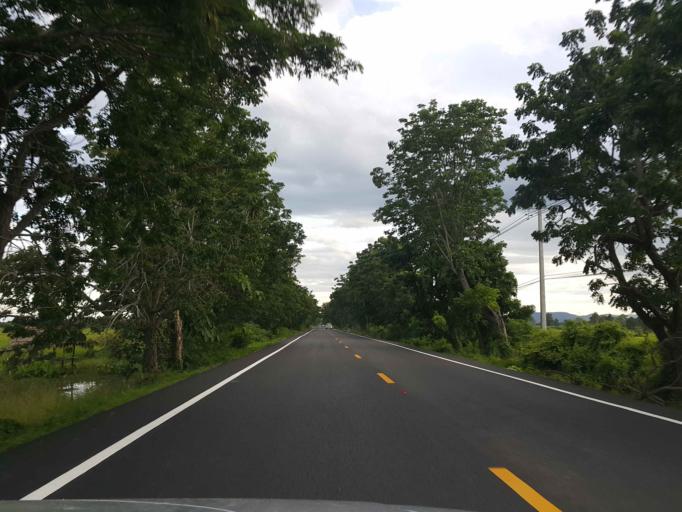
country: TH
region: Sukhothai
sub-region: Amphoe Si Satchanalai
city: Si Satchanalai
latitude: 17.4891
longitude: 99.7475
